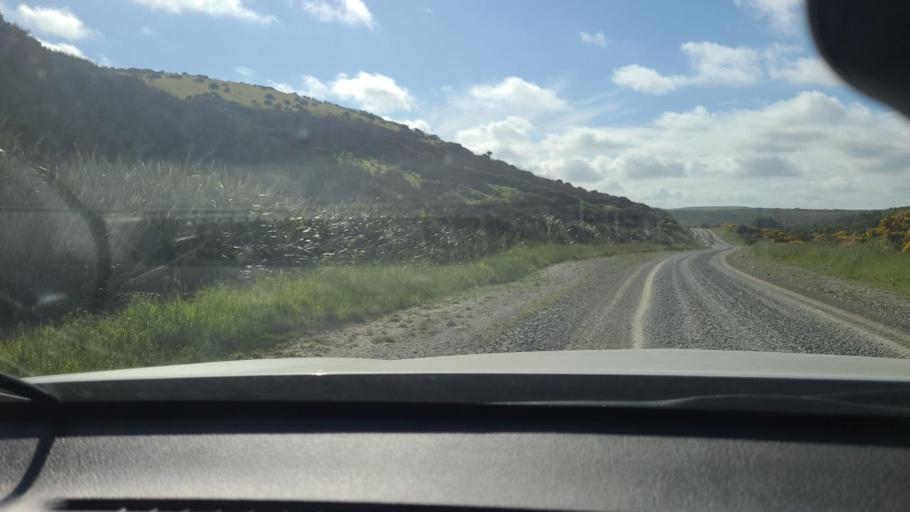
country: NZ
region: Southland
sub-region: Southland District
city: Winton
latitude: -45.8204
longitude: 168.2507
